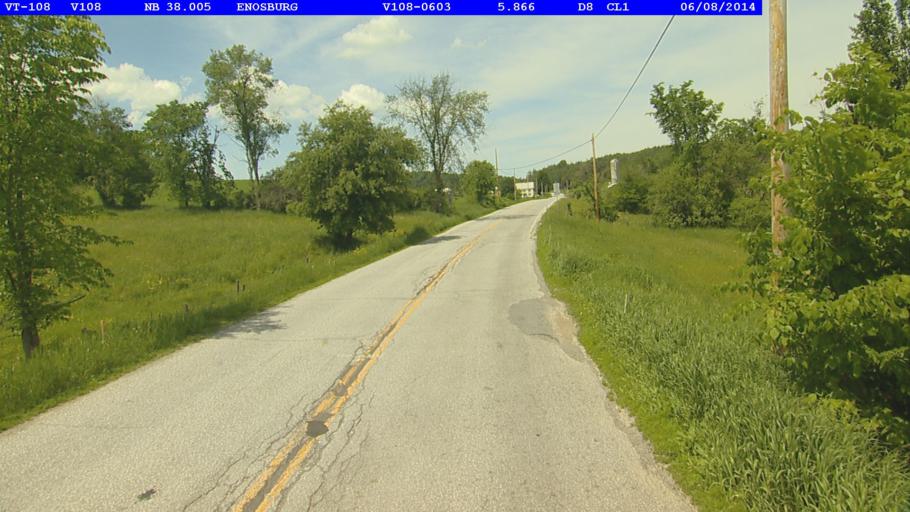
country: US
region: Vermont
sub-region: Franklin County
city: Enosburg Falls
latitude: 44.9245
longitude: -72.8092
